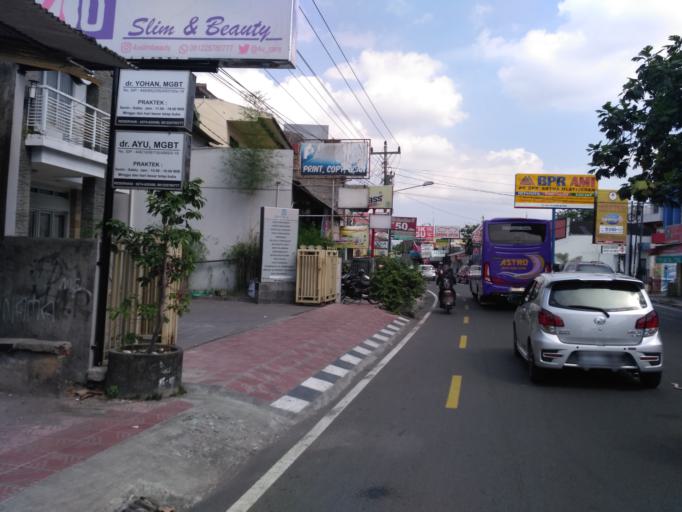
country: ID
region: Daerah Istimewa Yogyakarta
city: Melati
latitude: -7.7542
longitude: 110.3701
